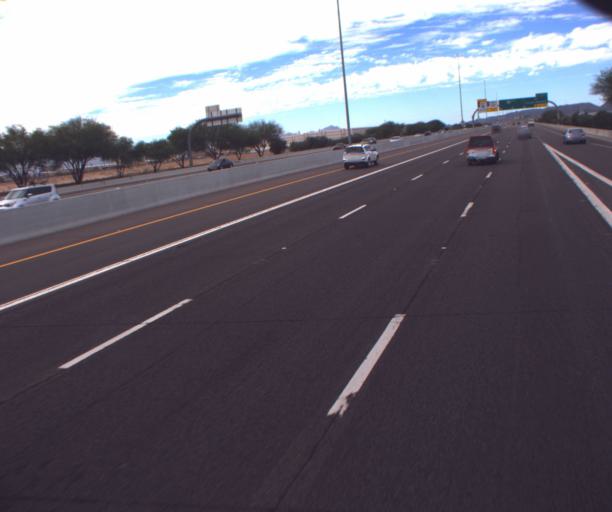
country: US
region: Arizona
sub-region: Maricopa County
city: Guadalupe
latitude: 33.2931
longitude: -111.9501
